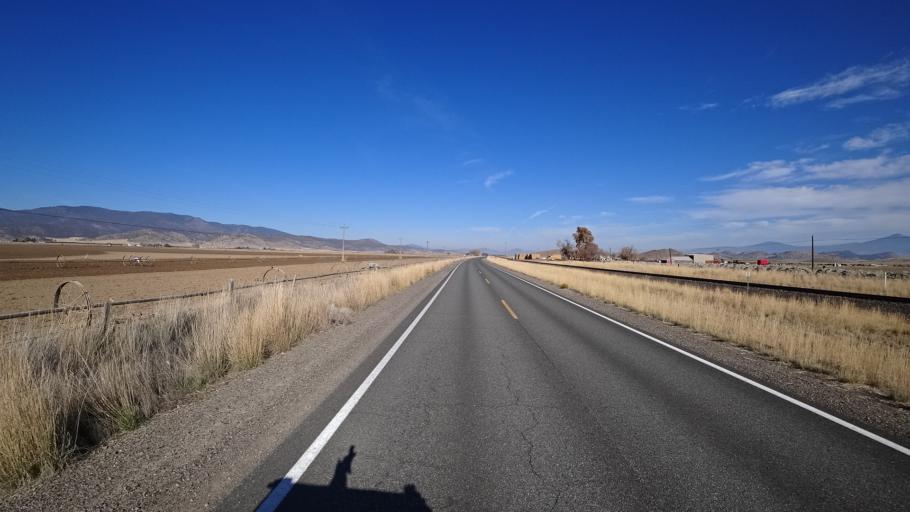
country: US
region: California
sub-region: Siskiyou County
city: Weed
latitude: 41.5417
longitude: -122.5256
